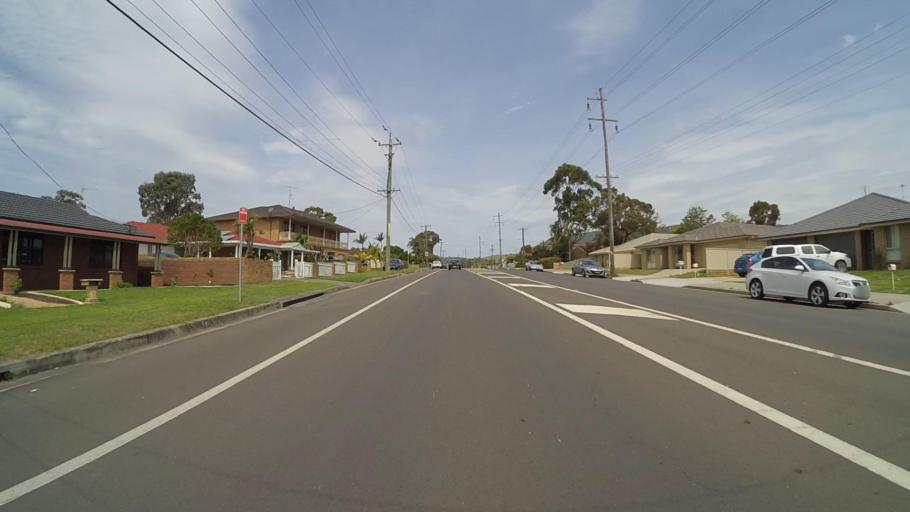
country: AU
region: New South Wales
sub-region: Shellharbour
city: Albion Park Rail
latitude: -34.5765
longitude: 150.7767
